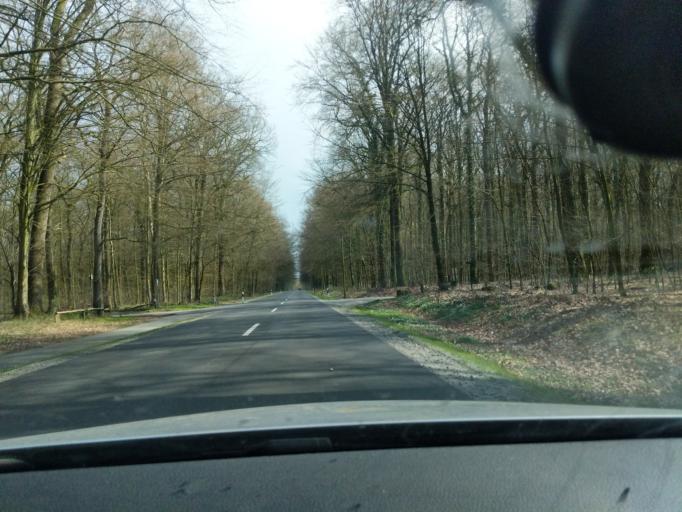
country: DE
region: Lower Saxony
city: Agathenburg
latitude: 53.5201
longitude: 9.4993
